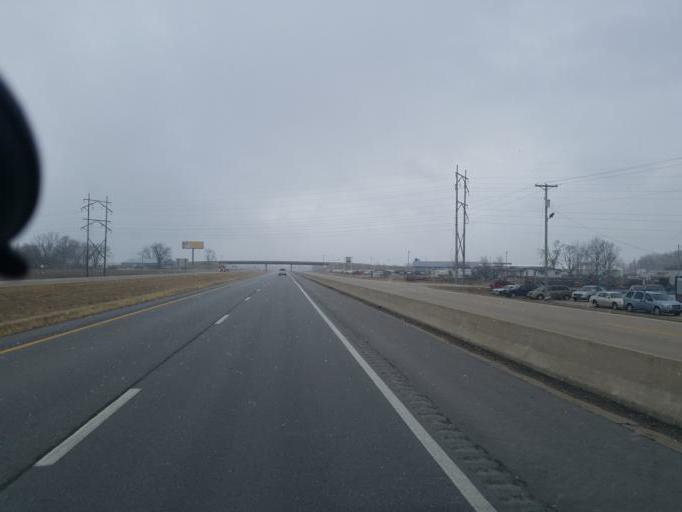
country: US
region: Missouri
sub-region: Randolph County
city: Moberly
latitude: 39.4345
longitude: -92.4181
